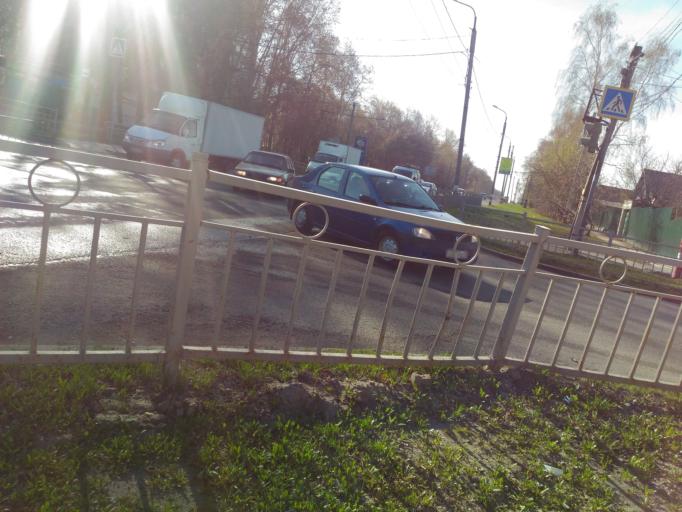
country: RU
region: Ulyanovsk
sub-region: Ulyanovskiy Rayon
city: Ulyanovsk
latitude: 54.3528
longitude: 48.3797
